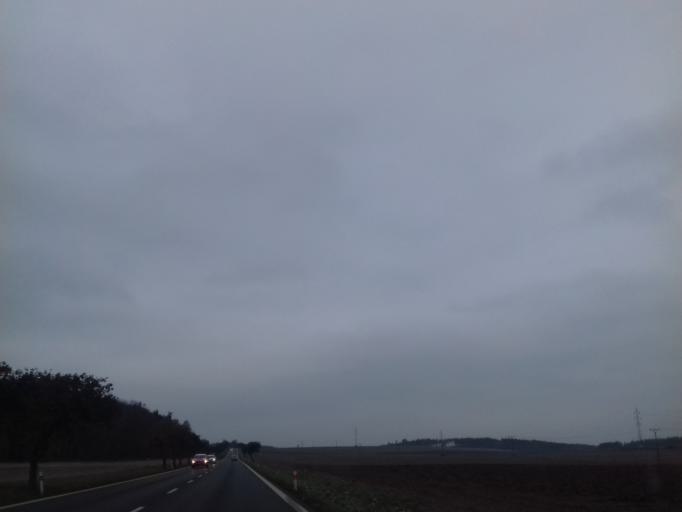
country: CZ
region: Plzensky
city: Stod
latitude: 49.6219
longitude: 13.1427
